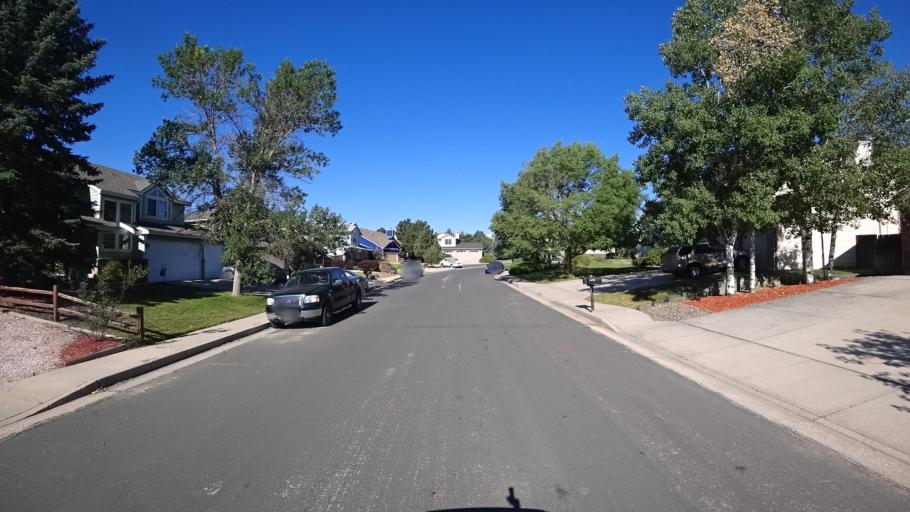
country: US
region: Colorado
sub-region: El Paso County
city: Black Forest
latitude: 38.9575
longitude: -104.7552
